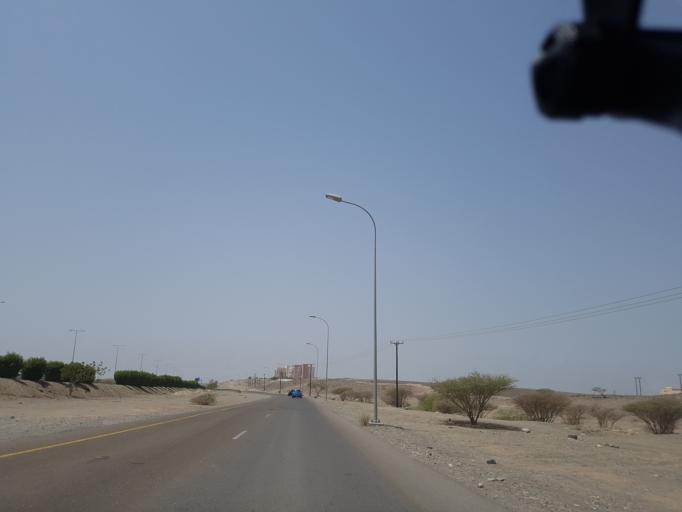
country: OM
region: Al Batinah
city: Al Liwa'
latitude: 24.4124
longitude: 56.5967
